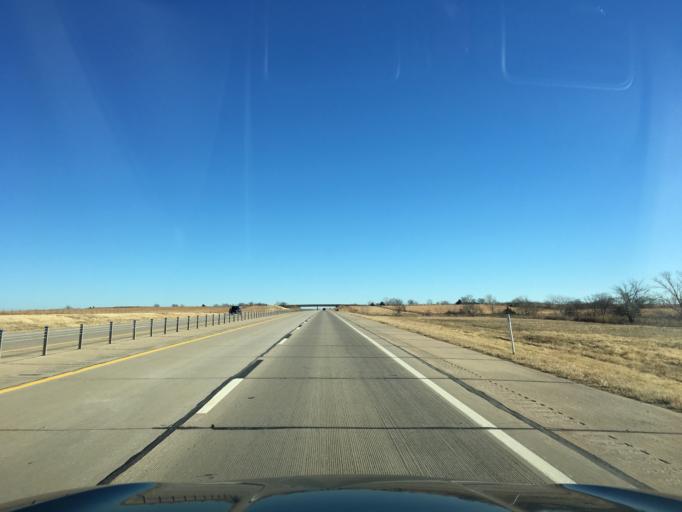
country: US
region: Oklahoma
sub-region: Noble County
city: Perry
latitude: 36.3933
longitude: -97.2014
